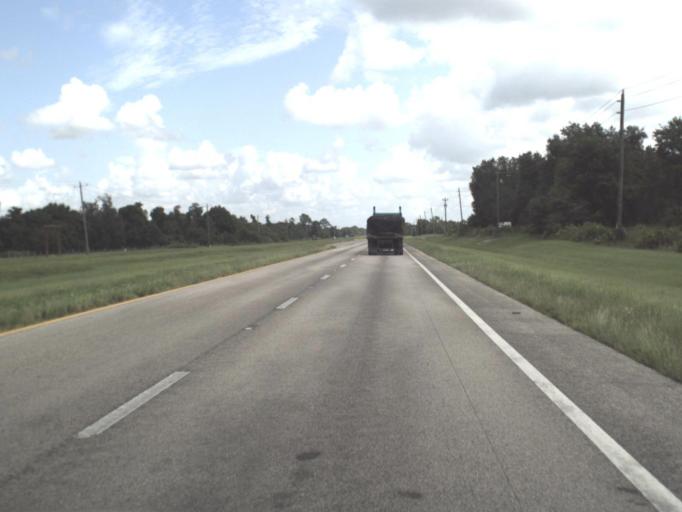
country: US
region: Florida
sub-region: DeSoto County
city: Arcadia
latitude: 27.3196
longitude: -81.8146
